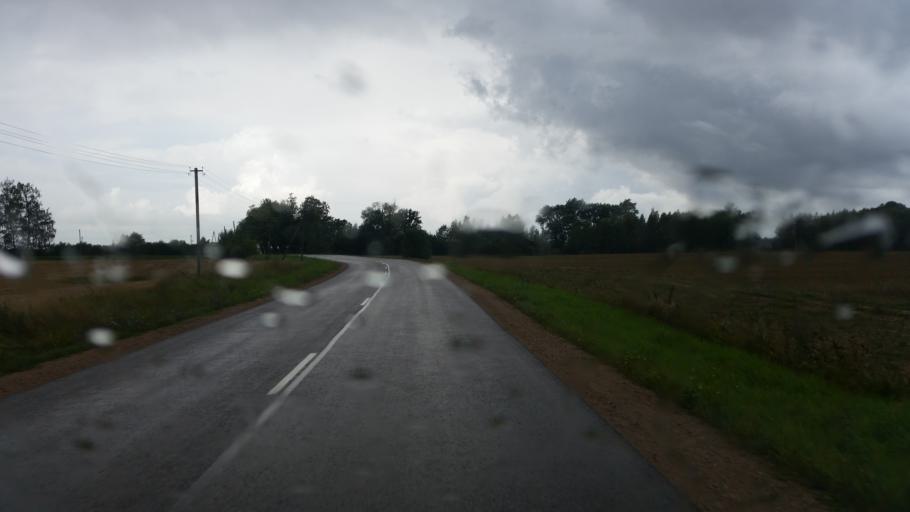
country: LV
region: Vecumnieki
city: Vecumnieki
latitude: 56.4329
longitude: 24.4153
